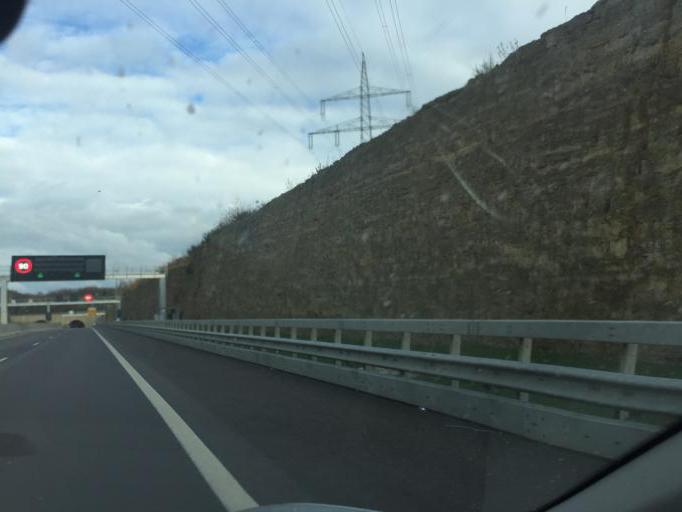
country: LU
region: Luxembourg
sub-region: Canton de Mersch
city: Lorentzweiler
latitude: 49.6849
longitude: 6.1613
